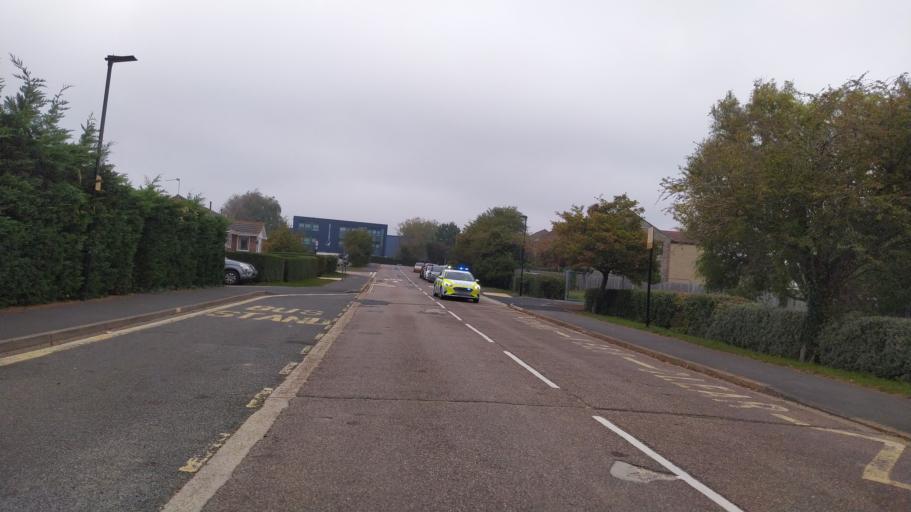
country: GB
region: England
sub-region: Isle of Wight
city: Newport
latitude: 50.6957
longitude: -1.3118
